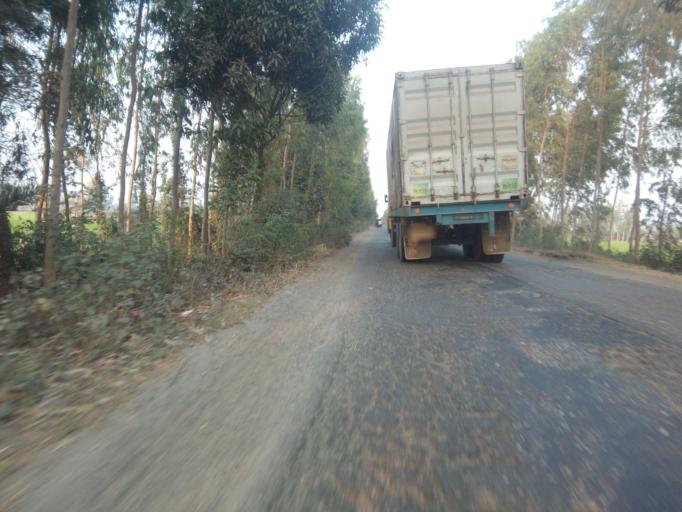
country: BD
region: Rajshahi
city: Bogra
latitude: 24.5623
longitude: 89.2046
